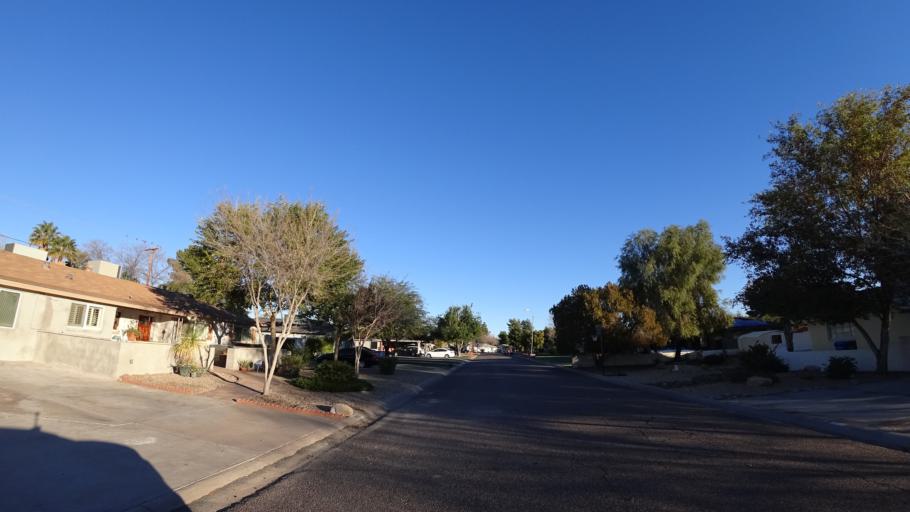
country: US
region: Arizona
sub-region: Maricopa County
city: Paradise Valley
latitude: 33.4917
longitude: -112.0060
